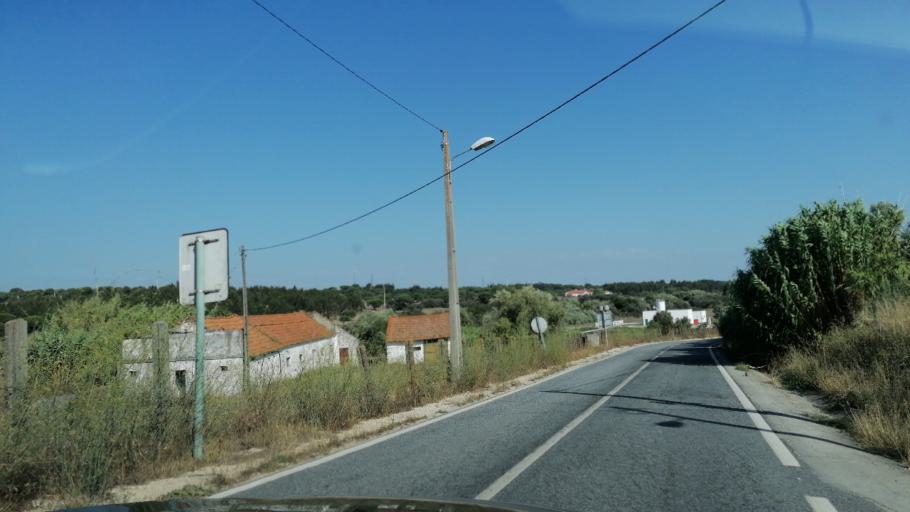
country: PT
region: Santarem
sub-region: Benavente
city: Poceirao
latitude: 38.7687
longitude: -8.6239
